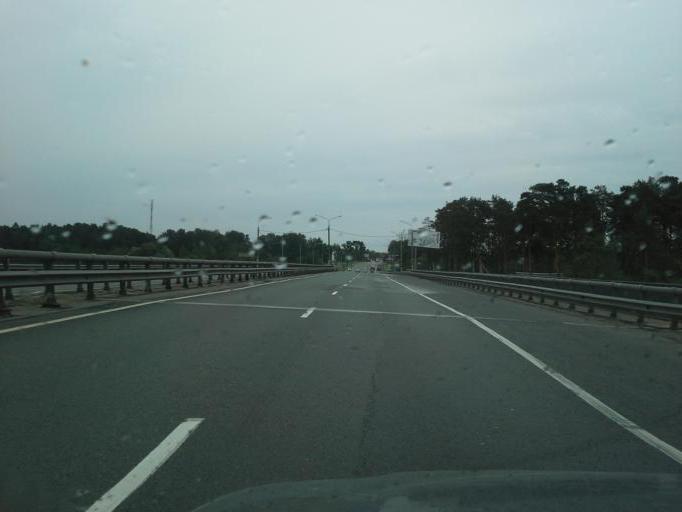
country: RU
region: Moskovskaya
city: Malaya Dubna
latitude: 55.8988
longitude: 39.0547
